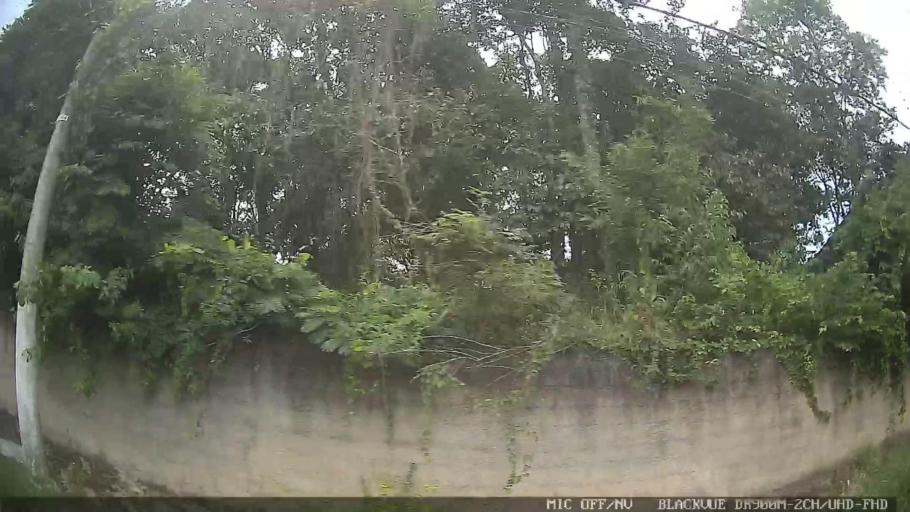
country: BR
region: Sao Paulo
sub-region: Atibaia
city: Atibaia
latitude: -23.1380
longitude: -46.5653
